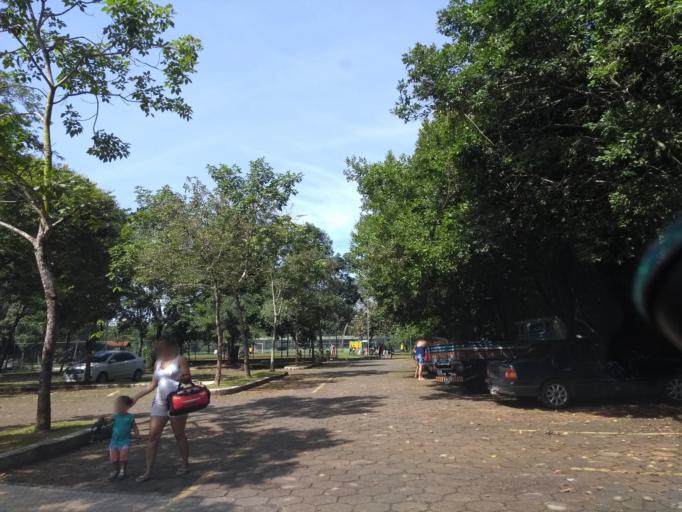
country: BR
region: Goias
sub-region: Goiania
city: Goiania
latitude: -16.6505
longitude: -49.2176
